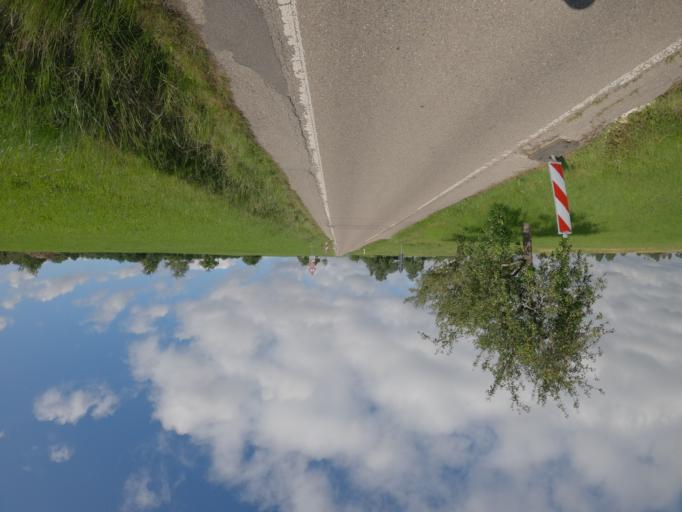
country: DE
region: Baden-Wuerttemberg
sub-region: Regierungsbezirk Stuttgart
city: Ebersbach an der Fils
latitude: 48.7300
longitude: 9.5390
